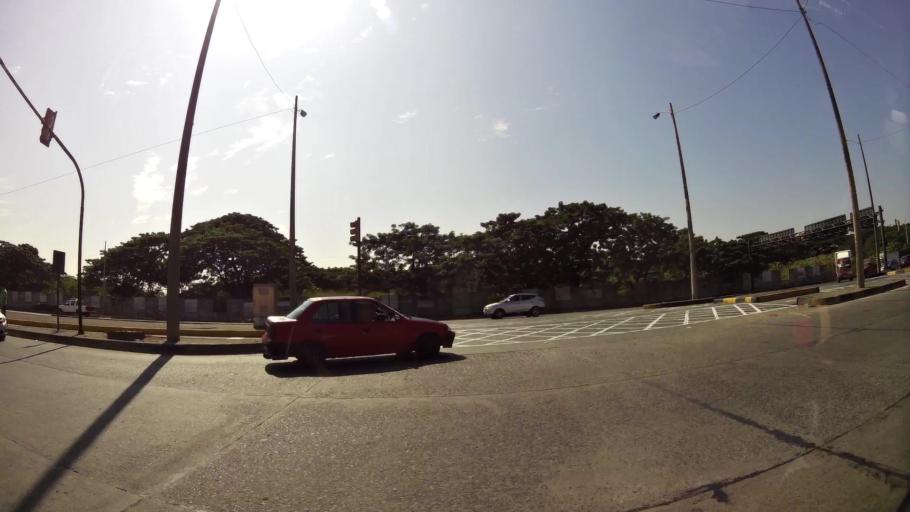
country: EC
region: Guayas
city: Guayaquil
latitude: -2.1153
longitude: -79.9329
